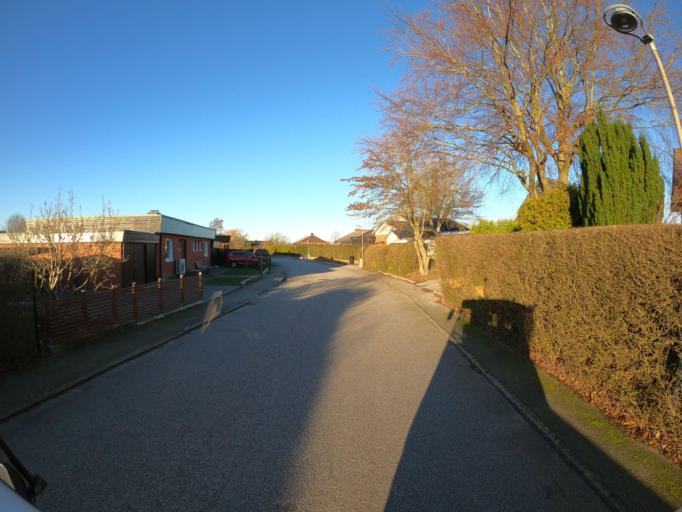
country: SE
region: Skane
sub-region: Svedala Kommun
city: Svedala
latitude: 55.5147
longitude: 13.2161
